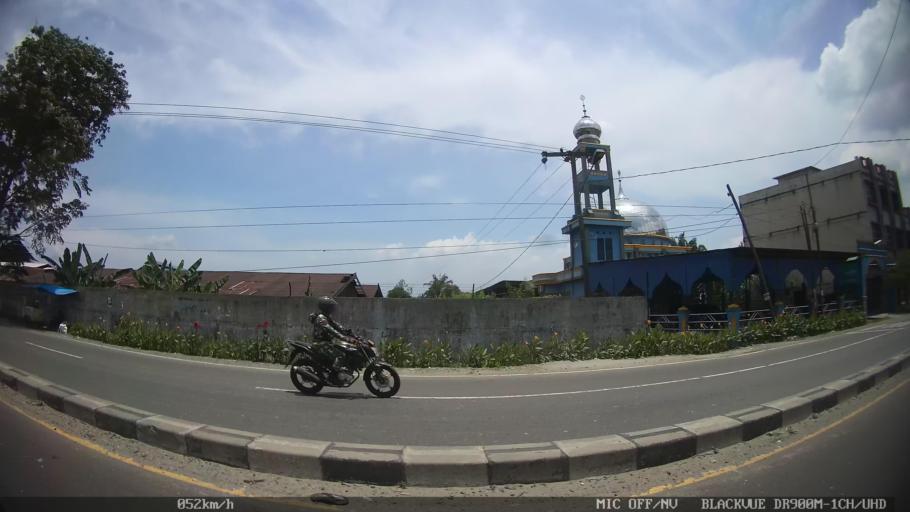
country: ID
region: North Sumatra
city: Binjai
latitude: 3.6026
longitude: 98.5388
